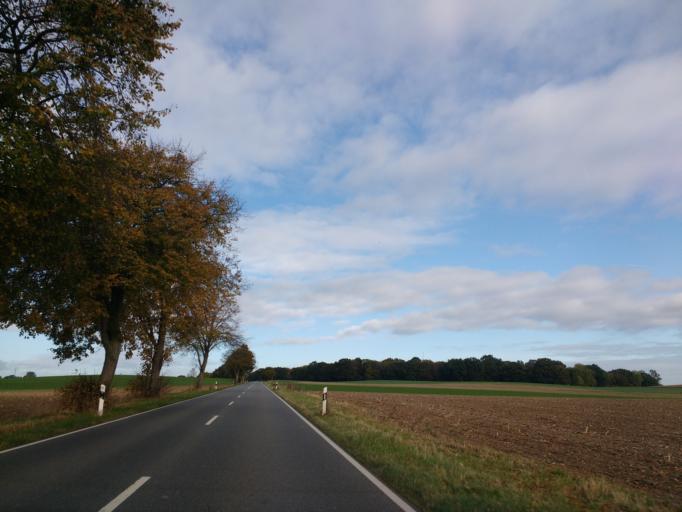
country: DE
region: Schleswig-Holstein
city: Altenkrempe
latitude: 54.1454
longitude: 10.8211
